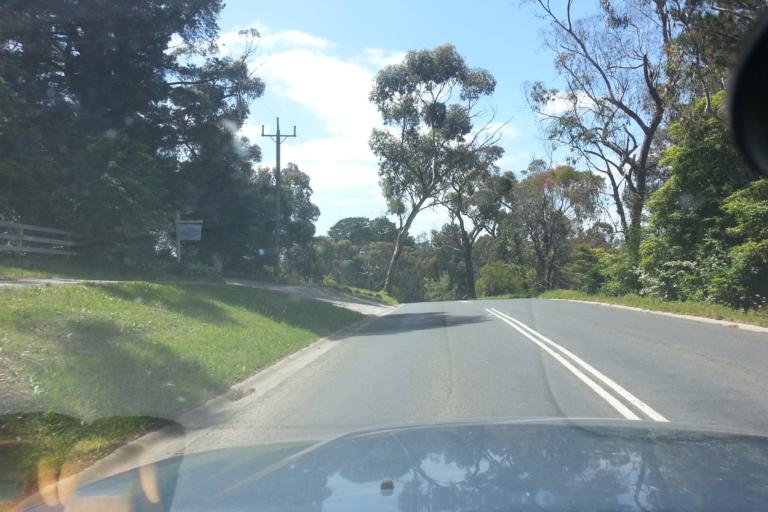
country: AU
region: Victoria
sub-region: Cardinia
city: Beaconsfield Upper
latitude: -38.0069
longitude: 145.4251
